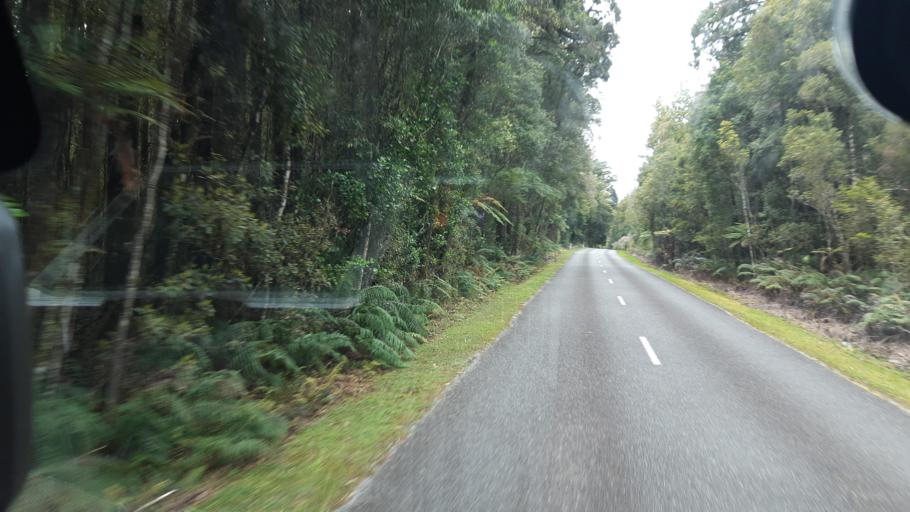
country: NZ
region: West Coast
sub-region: Westland District
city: Hokitika
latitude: -42.7792
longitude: 171.1029
